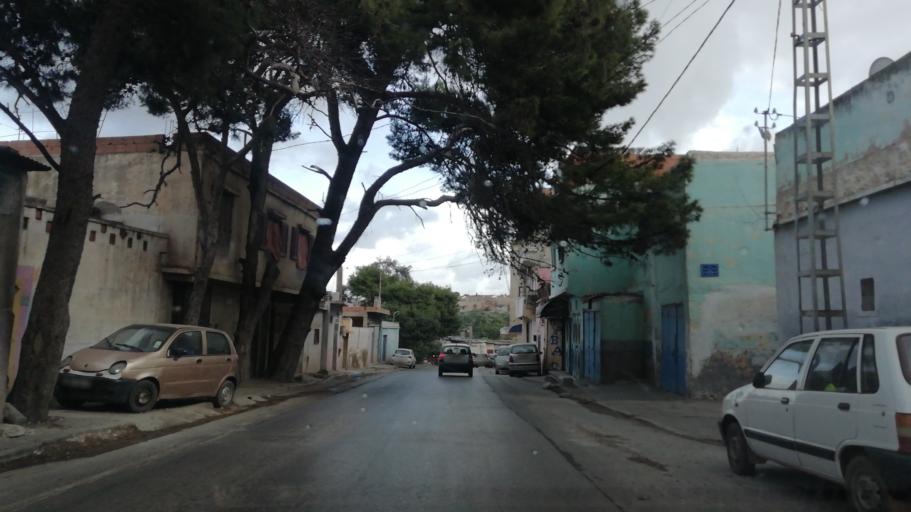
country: DZ
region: Oran
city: Oran
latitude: 35.6963
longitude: -0.6607
